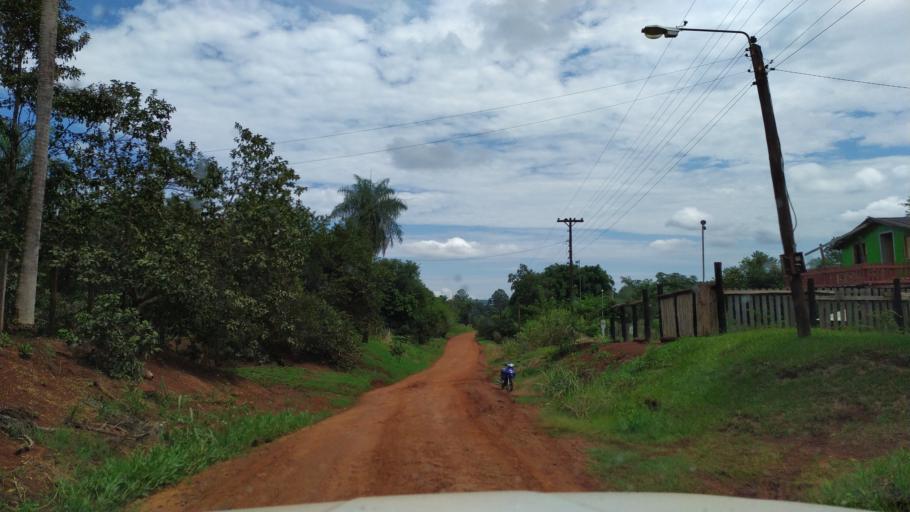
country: AR
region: Misiones
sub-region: Departamento de Eldorado
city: Eldorado
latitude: -26.5168
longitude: -54.5924
